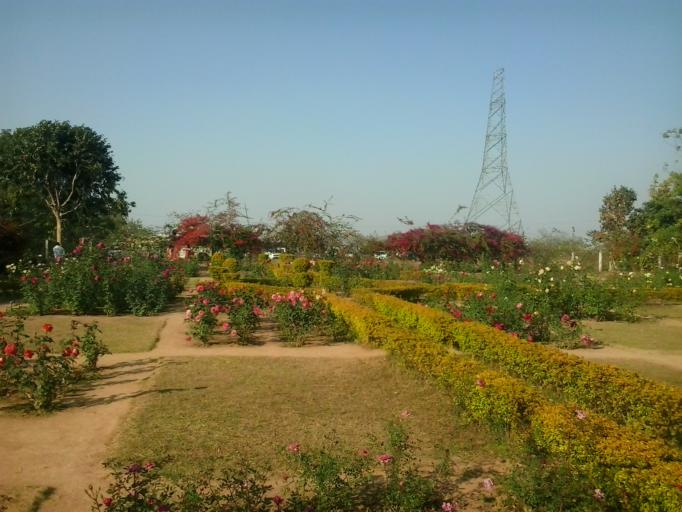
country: IN
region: Jharkhand
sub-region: Ranchi
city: Ranchi
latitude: 23.2539
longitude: 85.3469
